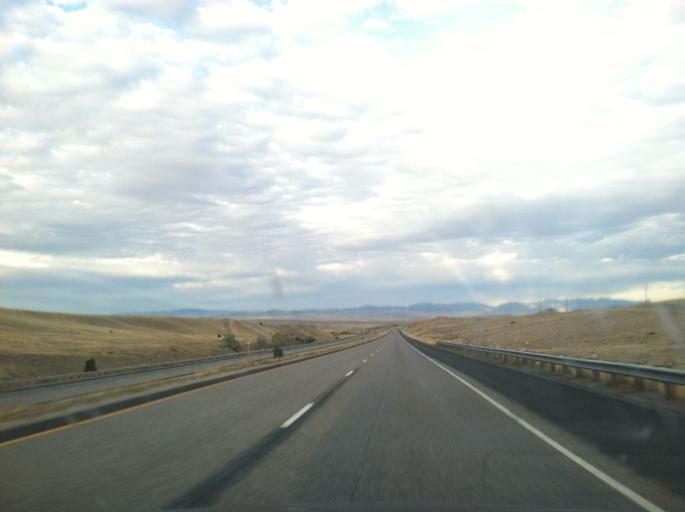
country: US
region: Montana
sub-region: Jefferson County
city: Whitehall
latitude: 45.8949
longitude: -111.8405
